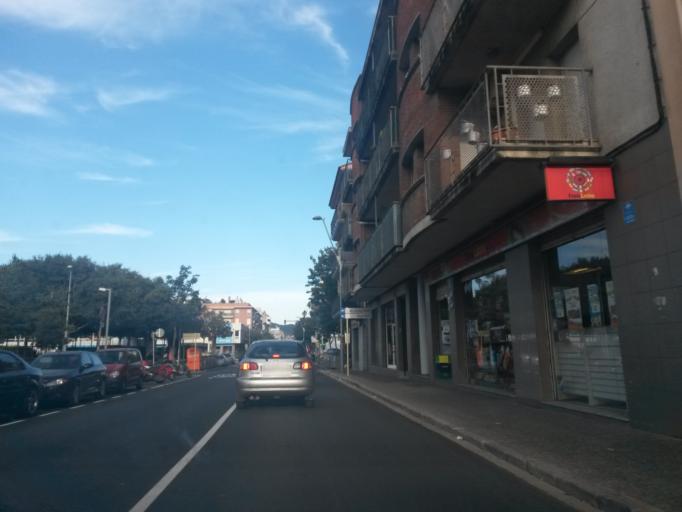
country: ES
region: Catalonia
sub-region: Provincia de Girona
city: Salt
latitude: 41.9774
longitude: 2.8070
